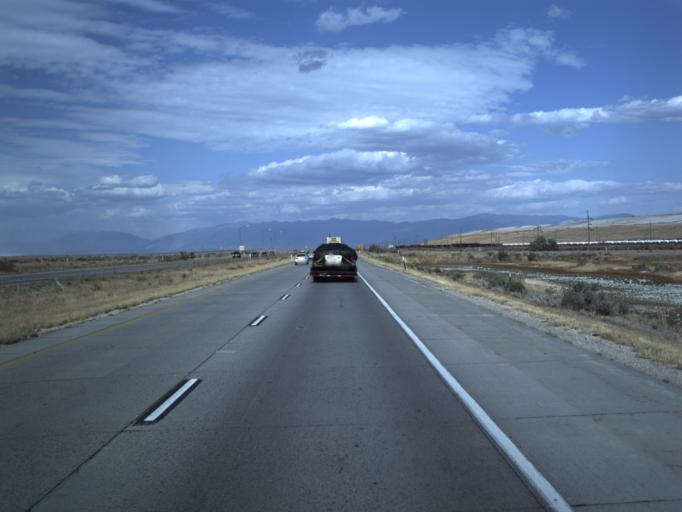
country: US
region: Utah
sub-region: Salt Lake County
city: Magna
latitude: 40.7461
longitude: -112.1819
